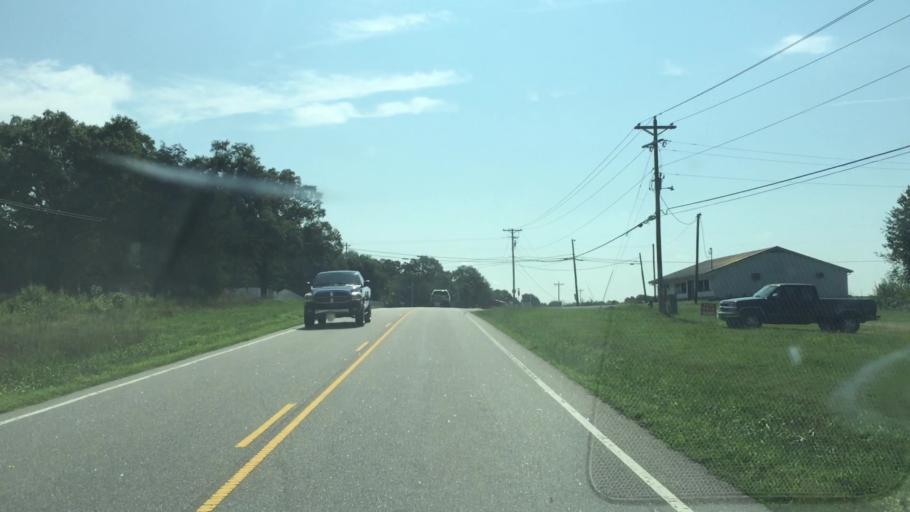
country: US
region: North Carolina
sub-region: Union County
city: Unionville
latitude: 35.1339
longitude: -80.4512
